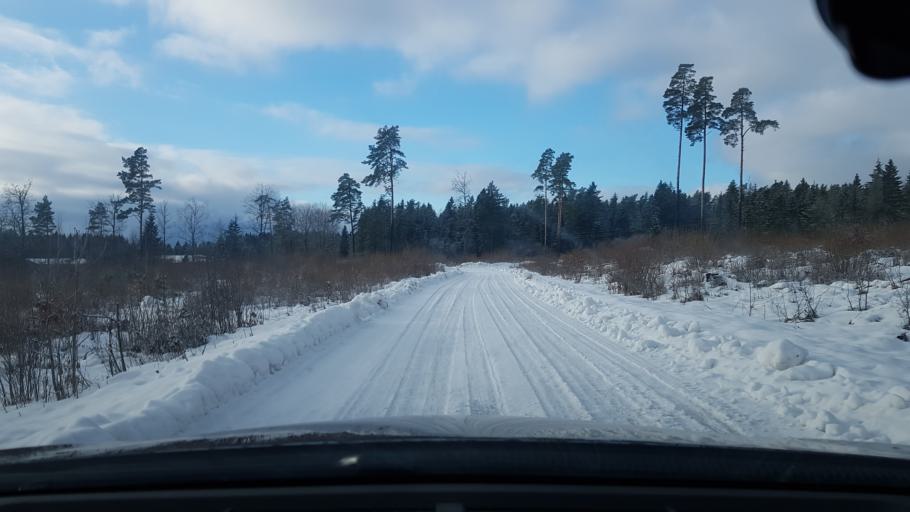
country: EE
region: Harju
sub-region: Keila linn
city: Keila
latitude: 59.2812
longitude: 24.2785
